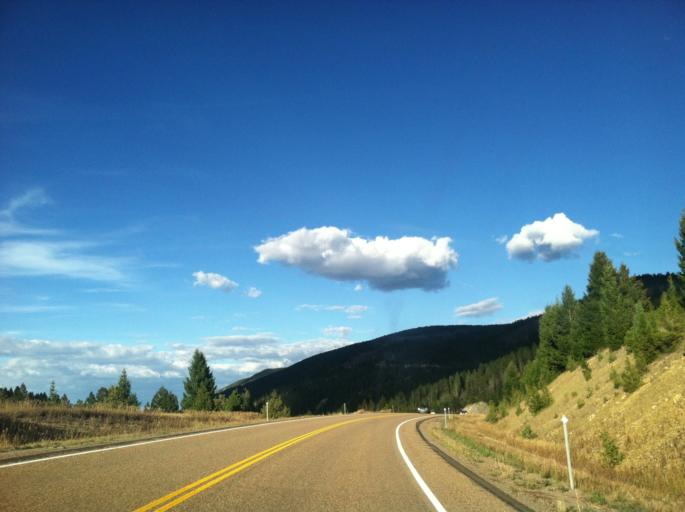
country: US
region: Montana
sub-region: Granite County
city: Philipsburg
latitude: 46.3991
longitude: -113.3045
